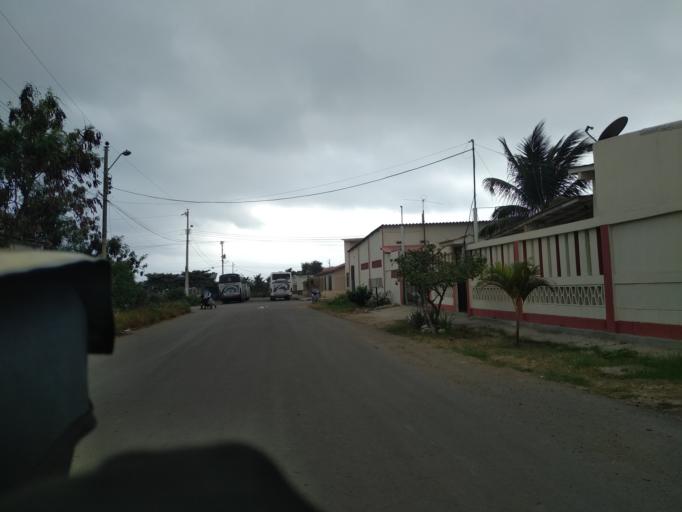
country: EC
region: Santa Elena
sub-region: Canton Santa Elena
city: Santa Elena
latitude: -2.2024
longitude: -80.8706
